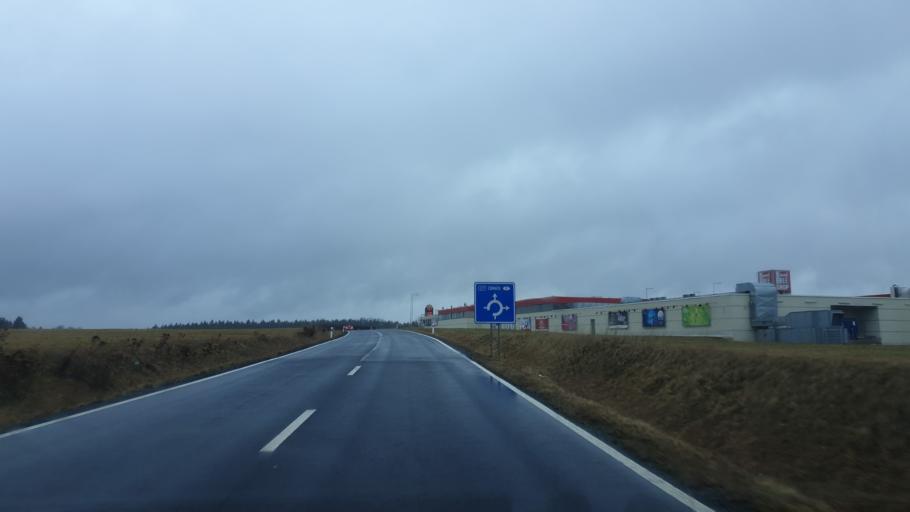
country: CZ
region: Karlovarsky
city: Hranice
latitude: 50.3158
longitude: 12.1668
